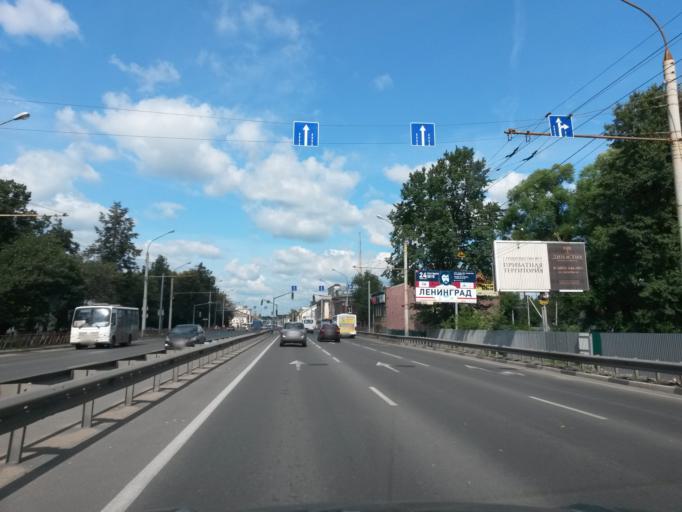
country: RU
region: Jaroslavl
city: Yaroslavl
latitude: 57.6077
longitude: 39.8801
